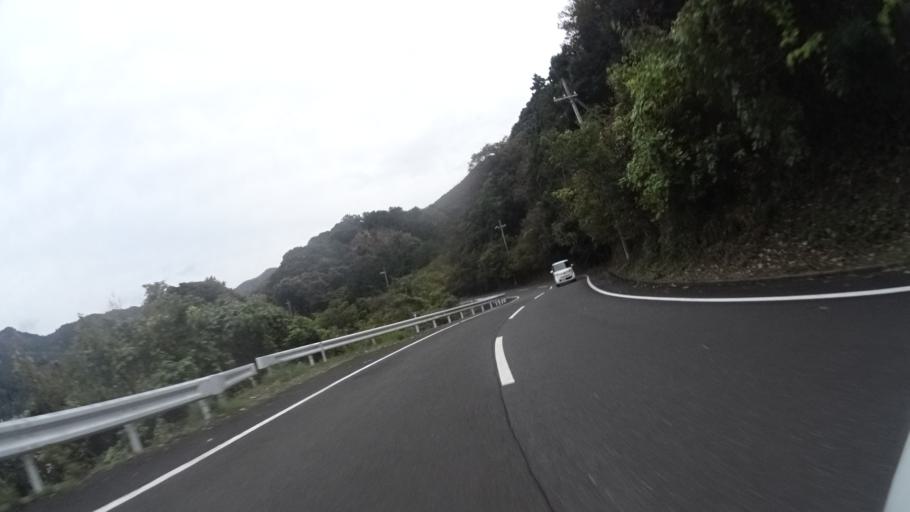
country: JP
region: Kyoto
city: Maizuru
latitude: 35.5714
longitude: 135.4498
